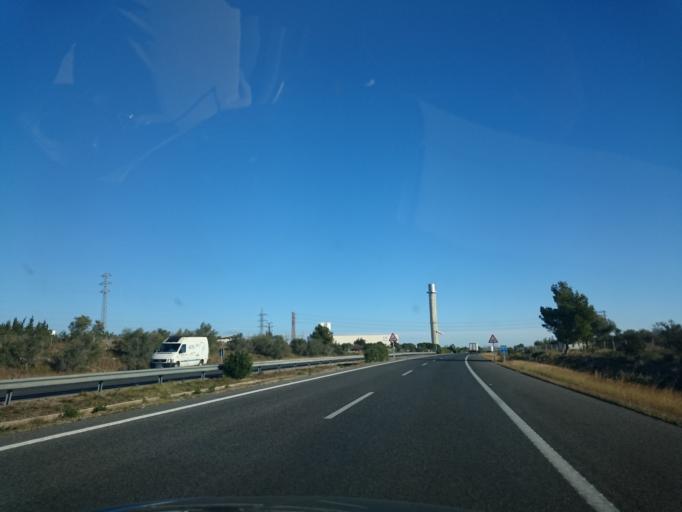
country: ES
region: Catalonia
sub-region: Provincia de Tarragona
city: Camarles
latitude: 40.7976
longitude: 0.6698
